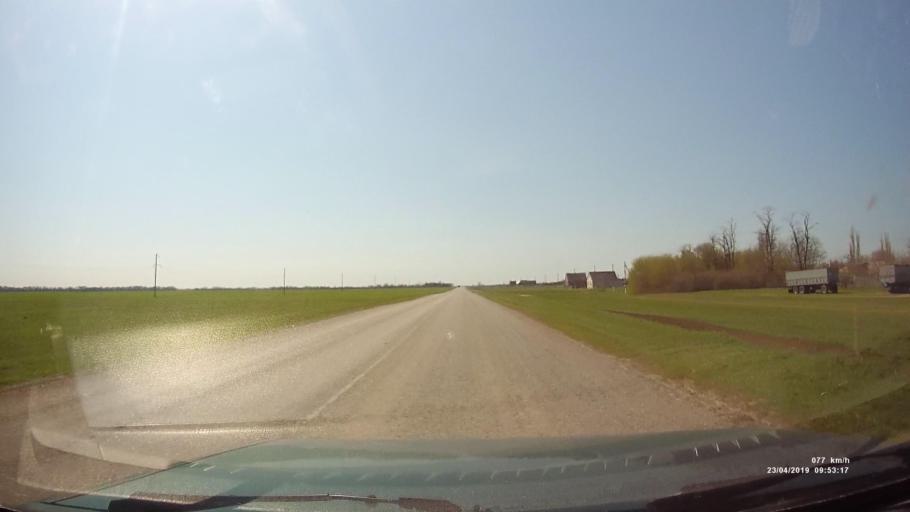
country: RU
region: Rostov
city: Orlovskiy
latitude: 46.8350
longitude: 42.0496
